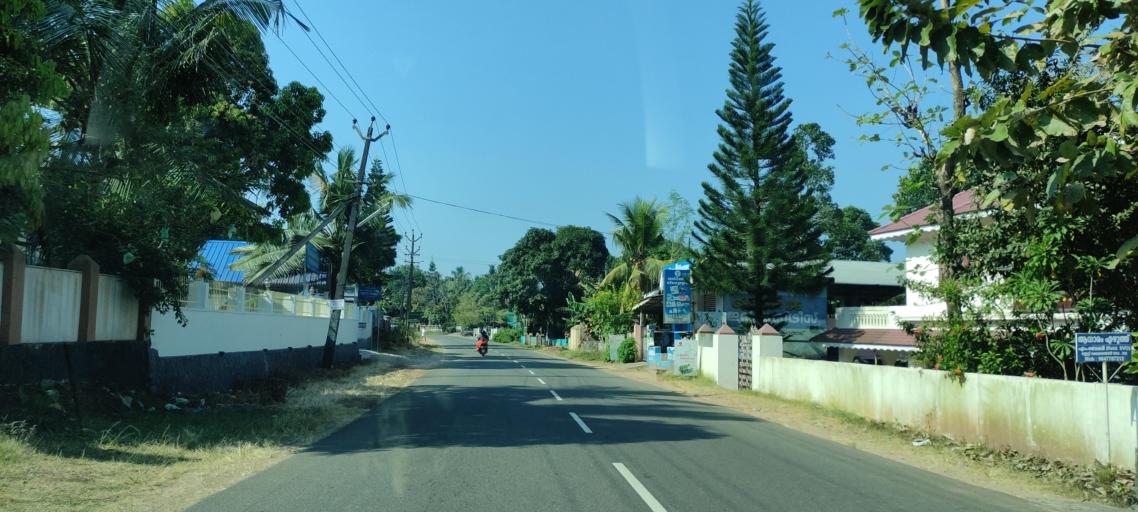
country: IN
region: Kerala
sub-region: Pattanamtitta
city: Adur
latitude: 9.1116
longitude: 76.6959
